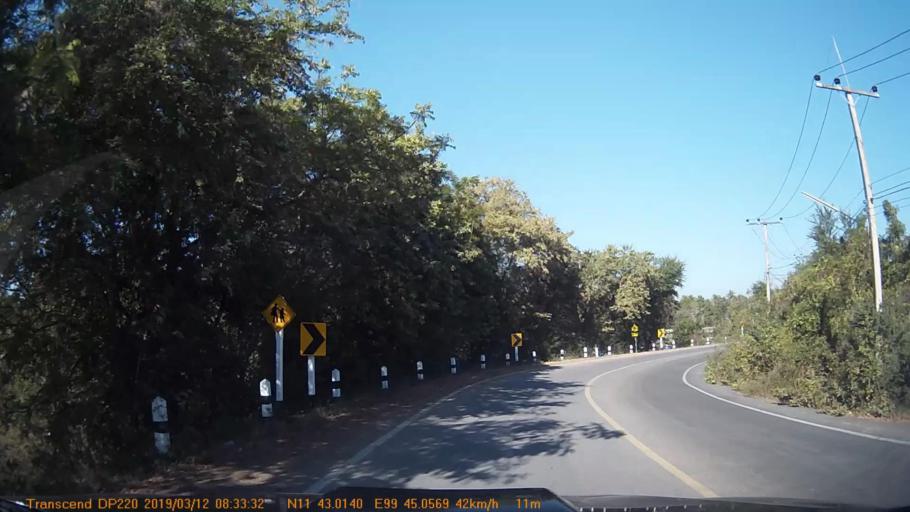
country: TH
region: Prachuap Khiri Khan
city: Prachuap Khiri Khan
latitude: 11.7167
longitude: 99.7513
